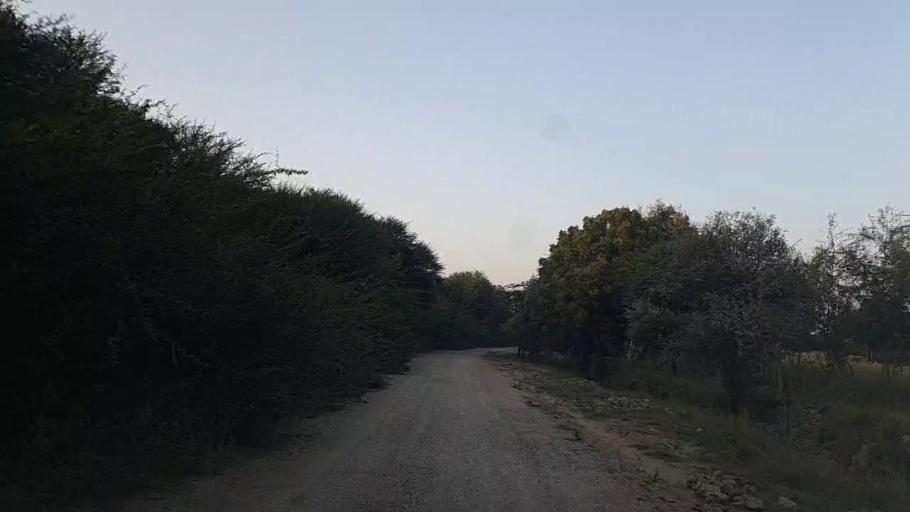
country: PK
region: Sindh
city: Naukot
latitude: 24.7005
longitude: 69.2732
